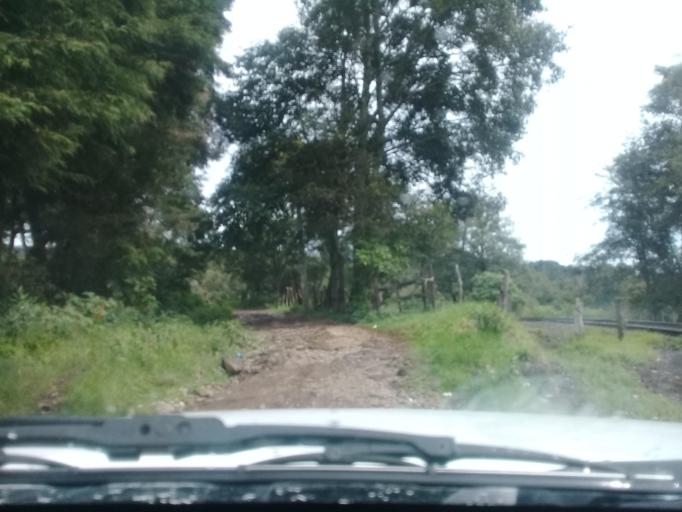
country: MX
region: Veracruz
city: Rafael Lucio
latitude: 19.5909
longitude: -96.9950
